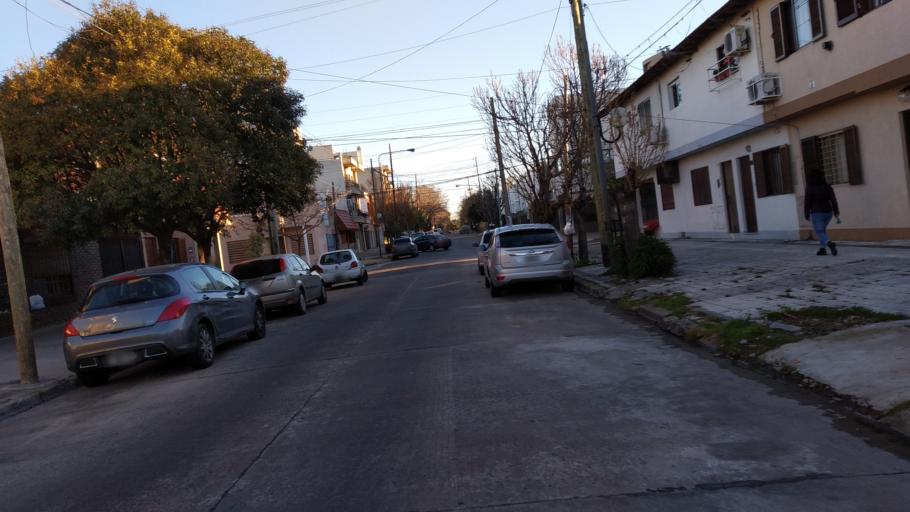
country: AR
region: Buenos Aires
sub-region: Partido de La Plata
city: La Plata
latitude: -34.9190
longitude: -57.9870
